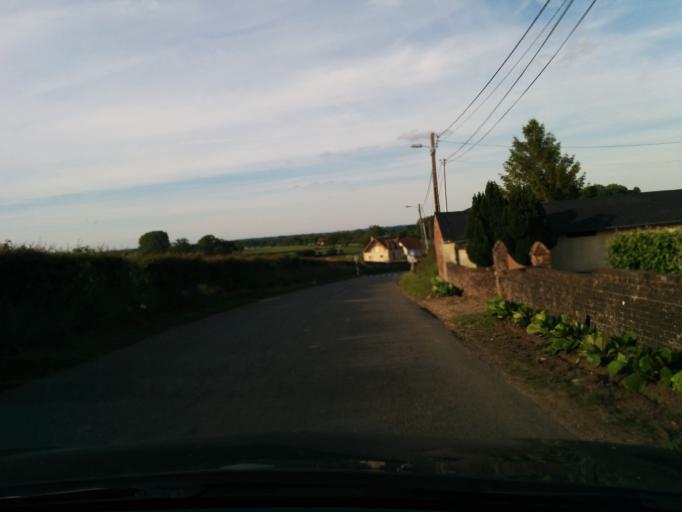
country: FR
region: Haute-Normandie
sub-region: Departement de la Seine-Maritime
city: Forges-les-Eaux
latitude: 49.5757
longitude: 1.4816
